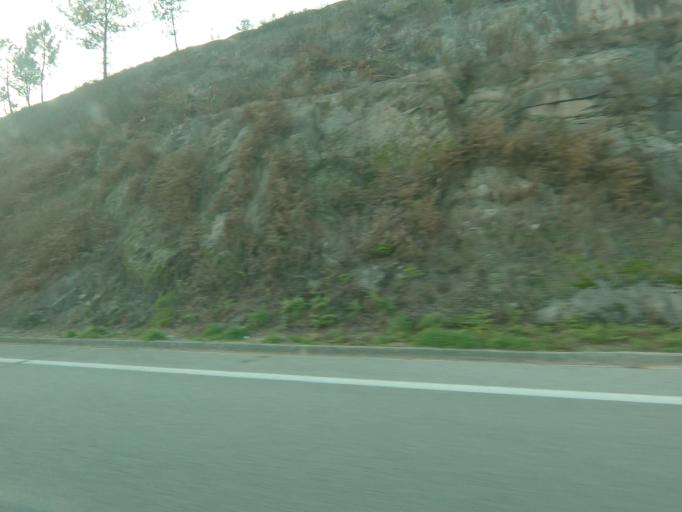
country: PT
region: Porto
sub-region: Amarante
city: Amarante
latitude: 41.2481
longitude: -8.1100
